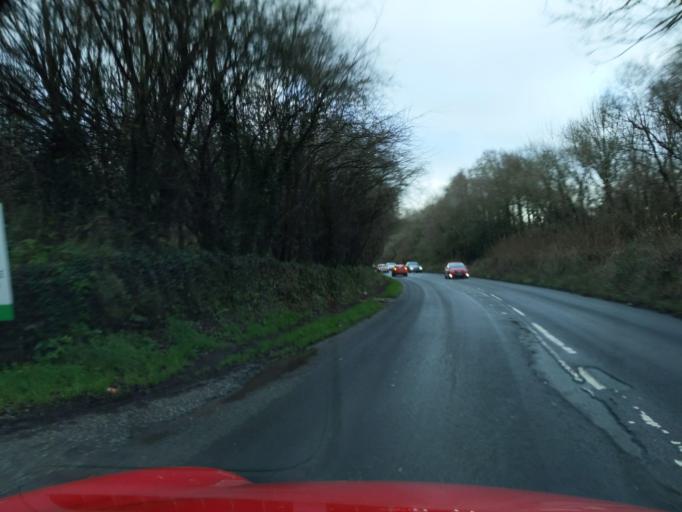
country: GB
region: England
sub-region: Devon
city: Plympton
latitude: 50.3673
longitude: -4.0665
